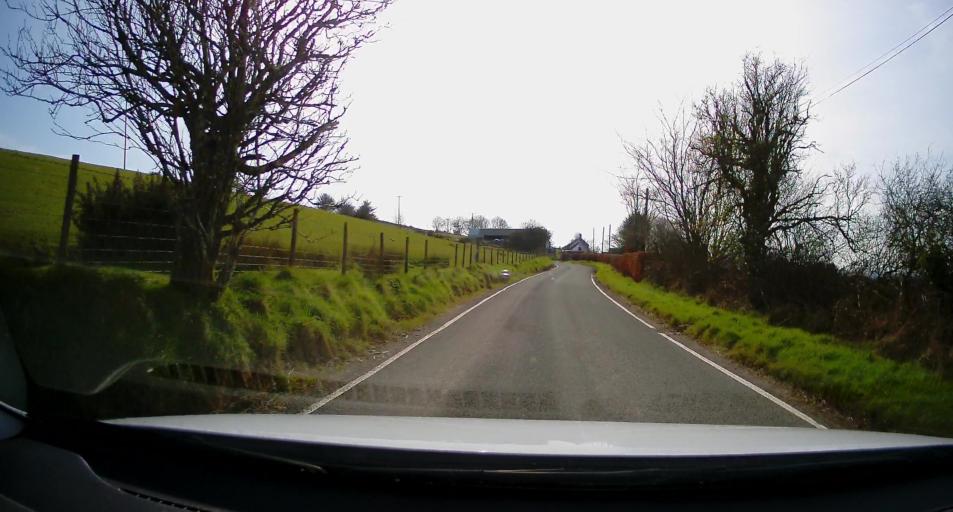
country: GB
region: Wales
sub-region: County of Ceredigion
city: Llanon
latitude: 52.2559
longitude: -4.0816
